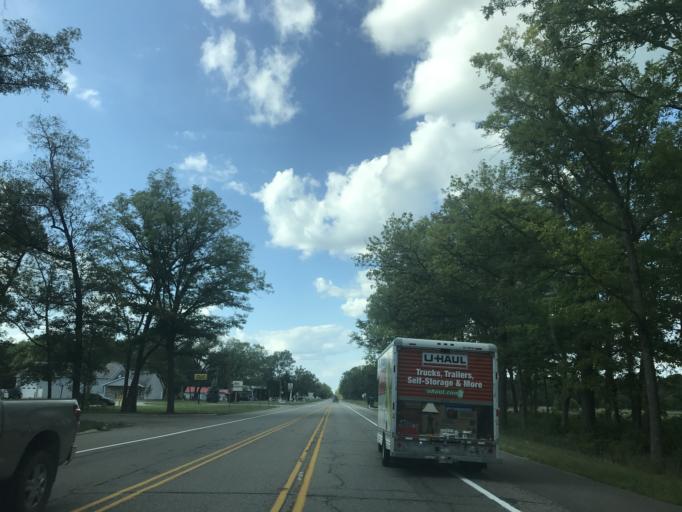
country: US
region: Michigan
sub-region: Newaygo County
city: White Cloud
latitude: 43.4831
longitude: -85.7734
